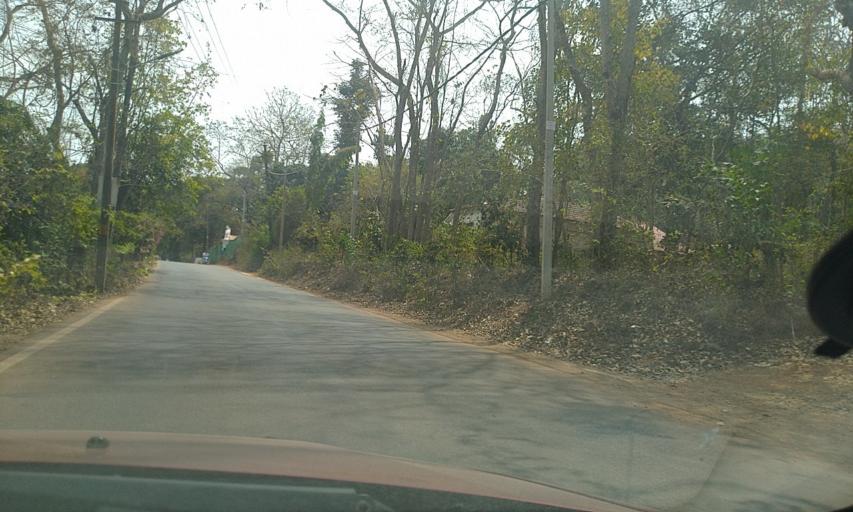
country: IN
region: Goa
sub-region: North Goa
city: Mapuca
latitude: 15.5971
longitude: 73.7863
